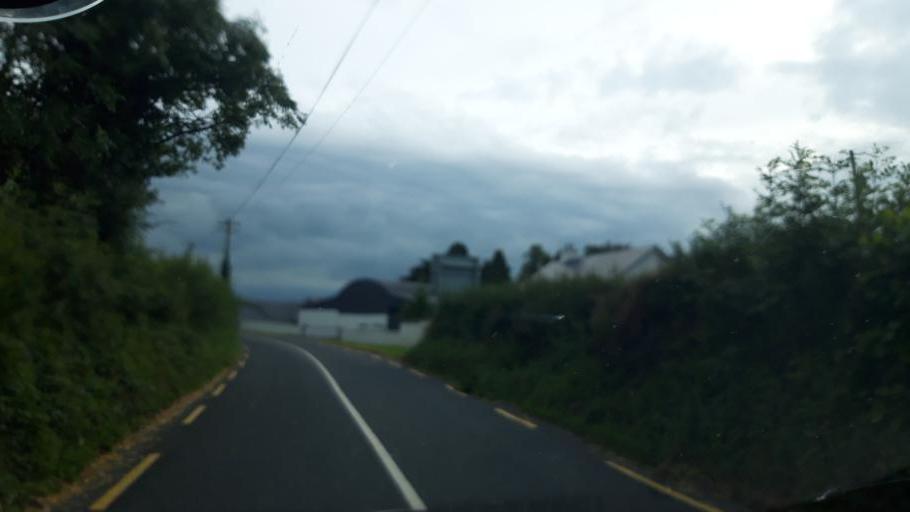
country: IE
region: Leinster
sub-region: Kilkenny
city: Ballyragget
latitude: 52.7549
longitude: -7.3917
